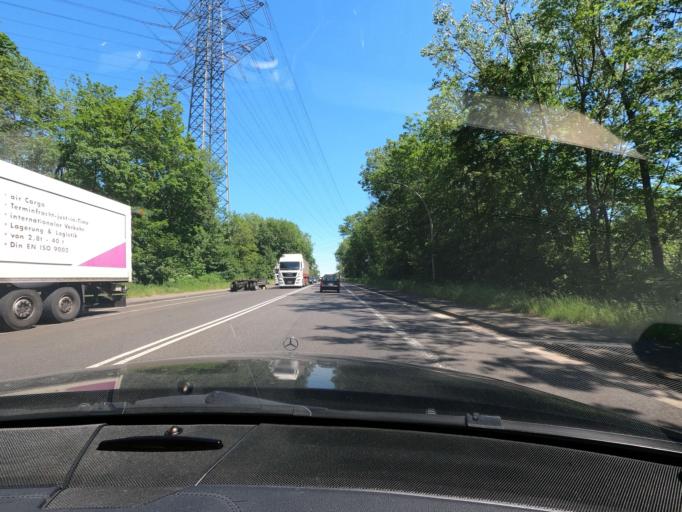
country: DE
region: North Rhine-Westphalia
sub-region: Regierungsbezirk Dusseldorf
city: Hochfeld
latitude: 51.3625
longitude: 6.7027
